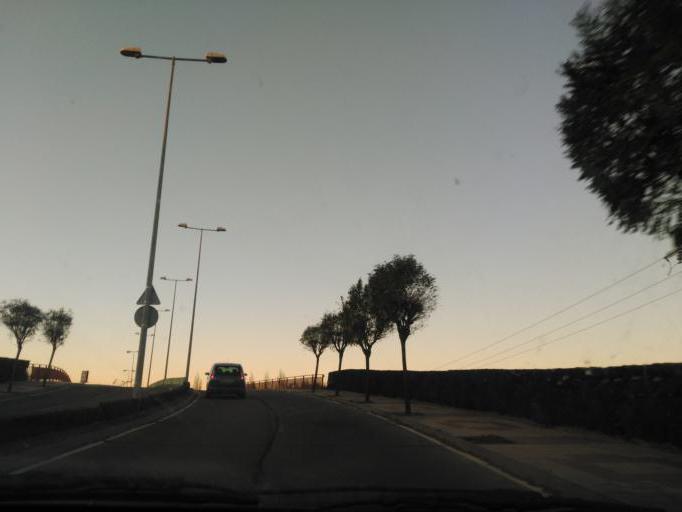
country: ES
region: Castille and Leon
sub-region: Provincia de Salamanca
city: Carbajosa de la Sagrada
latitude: 40.9372
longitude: -5.6519
